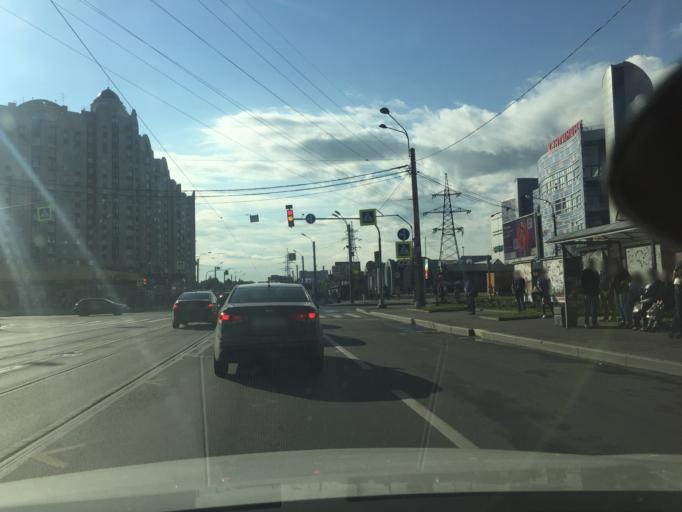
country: RU
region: St.-Petersburg
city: Kupchino
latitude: 59.8338
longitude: 30.3473
